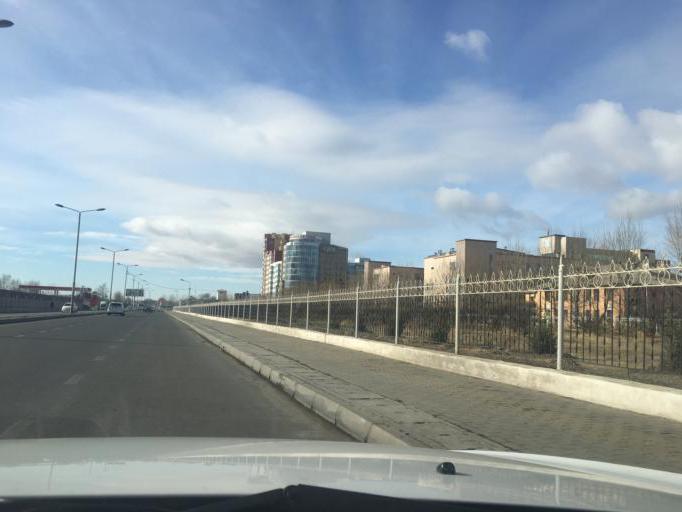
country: MN
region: Ulaanbaatar
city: Ulaanbaatar
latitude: 47.9093
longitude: 106.8813
